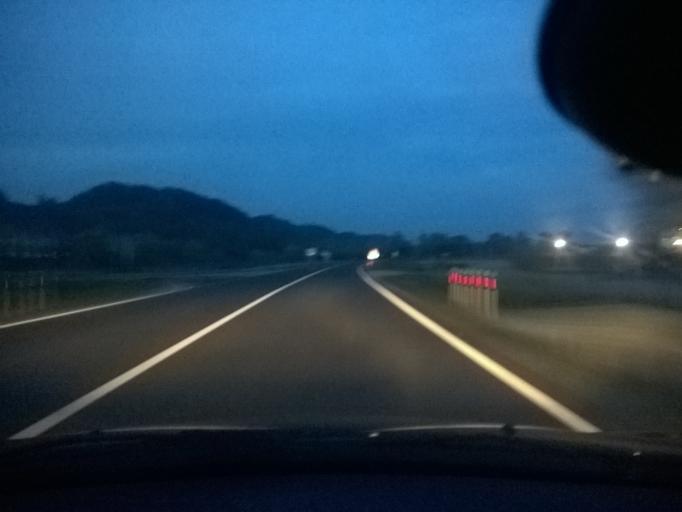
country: HR
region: Zagrebacka
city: Jakovlje
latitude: 45.9576
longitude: 15.8293
